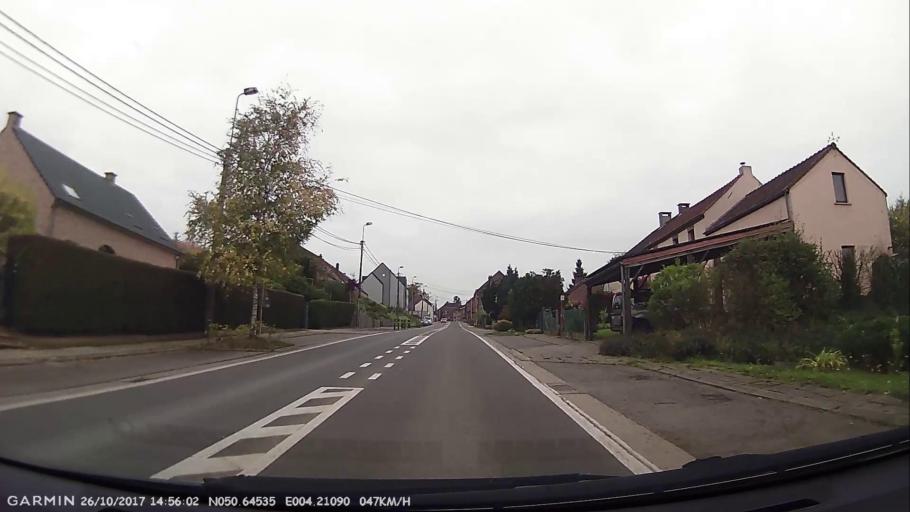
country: BE
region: Wallonia
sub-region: Province du Brabant Wallon
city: Tubize
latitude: 50.6453
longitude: 4.2107
